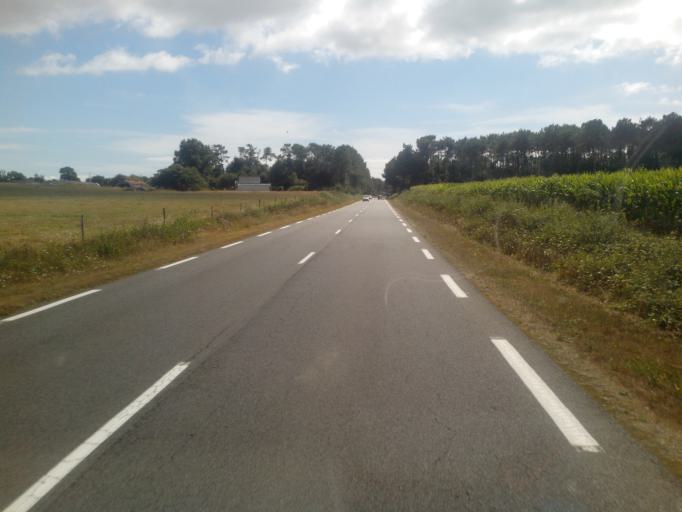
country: FR
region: Brittany
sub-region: Departement du Morbihan
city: Peaule
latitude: 47.5830
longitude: -2.3776
